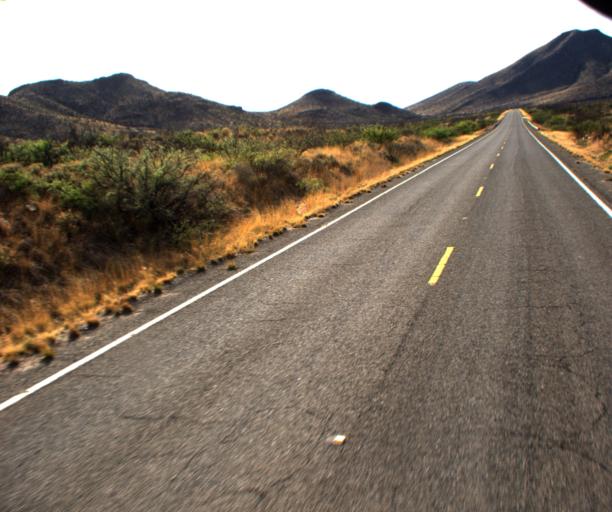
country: US
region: Arizona
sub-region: Cochise County
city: Willcox
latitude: 32.1804
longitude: -109.6354
